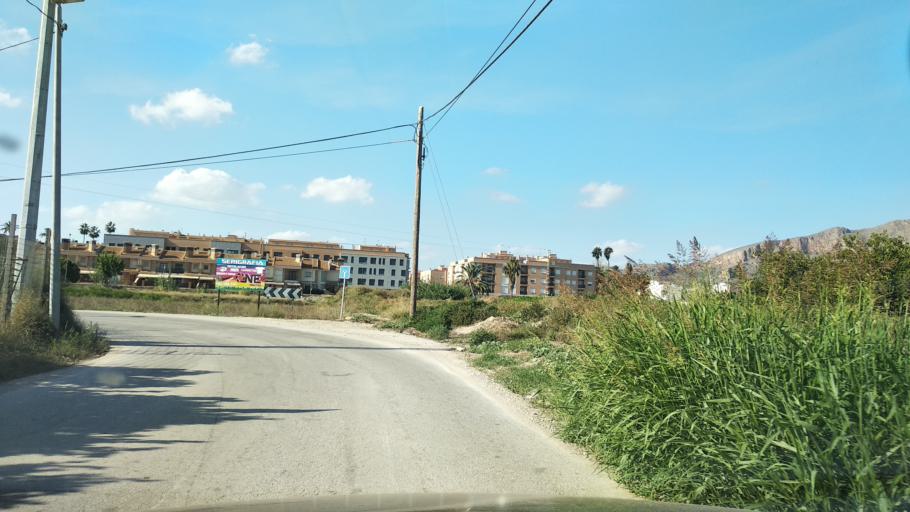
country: ES
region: Murcia
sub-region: Murcia
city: Santomera
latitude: 38.0577
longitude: -1.0441
